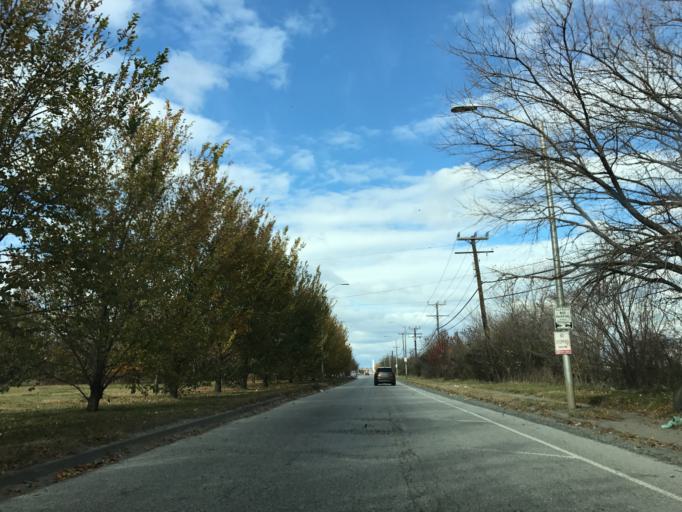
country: US
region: Maryland
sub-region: Anne Arundel County
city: Brooklyn Park
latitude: 39.2429
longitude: -76.6079
